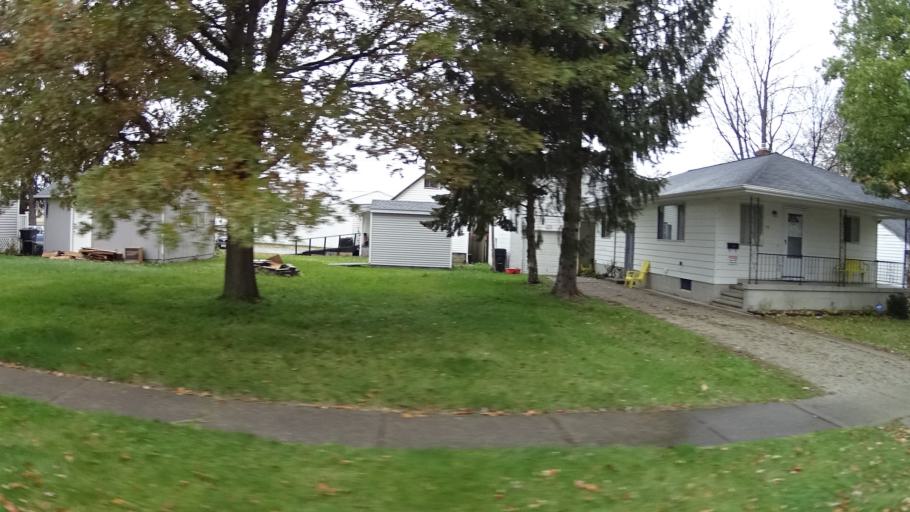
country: US
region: Ohio
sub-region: Lorain County
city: Elyria
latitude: 41.3757
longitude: -82.1294
